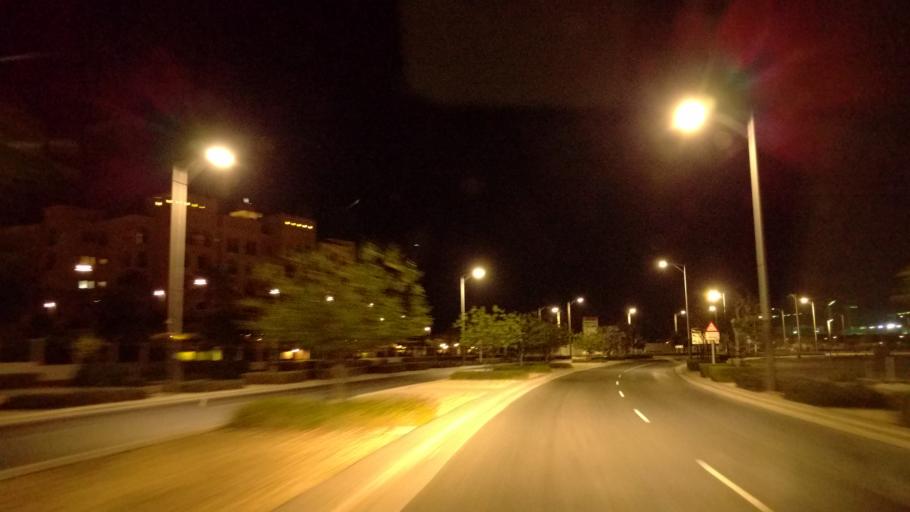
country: AE
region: Abu Dhabi
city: Abu Dhabi
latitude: 24.5520
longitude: 54.4529
